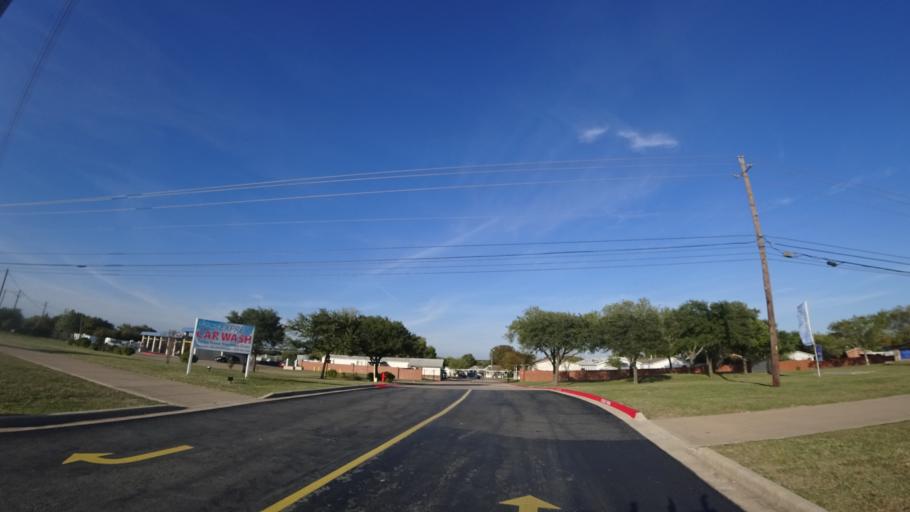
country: US
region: Texas
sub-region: Travis County
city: Wells Branch
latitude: 30.4142
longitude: -97.6541
